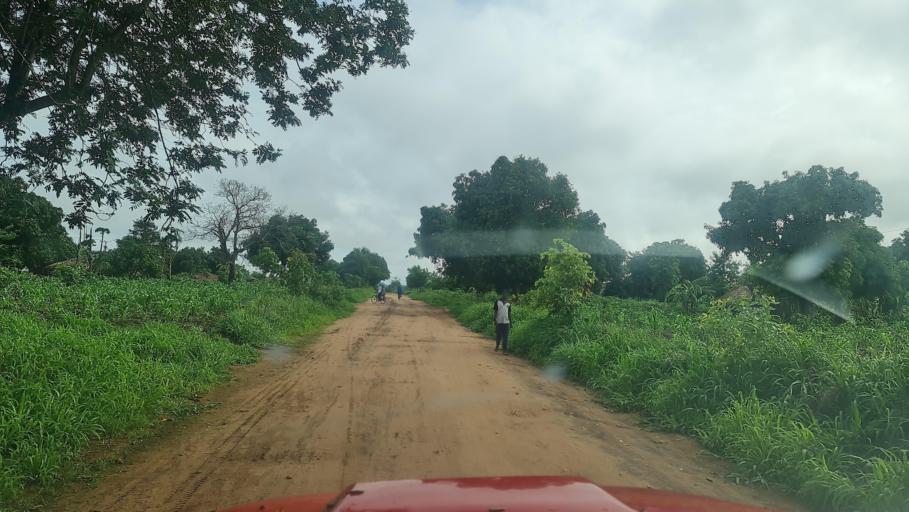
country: MW
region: Southern Region
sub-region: Nsanje District
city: Nsanje
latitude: -17.2838
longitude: 35.6117
